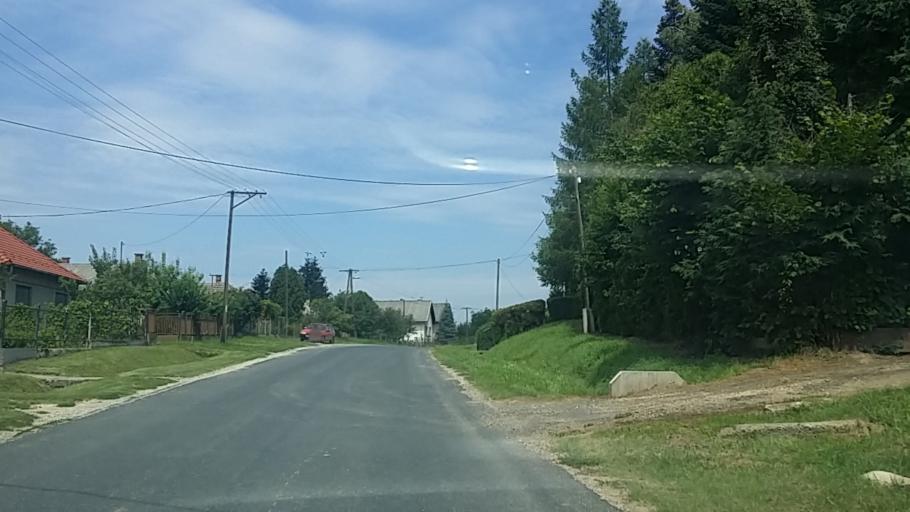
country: HR
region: Medimurska
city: Podturen
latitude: 46.5321
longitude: 16.5884
